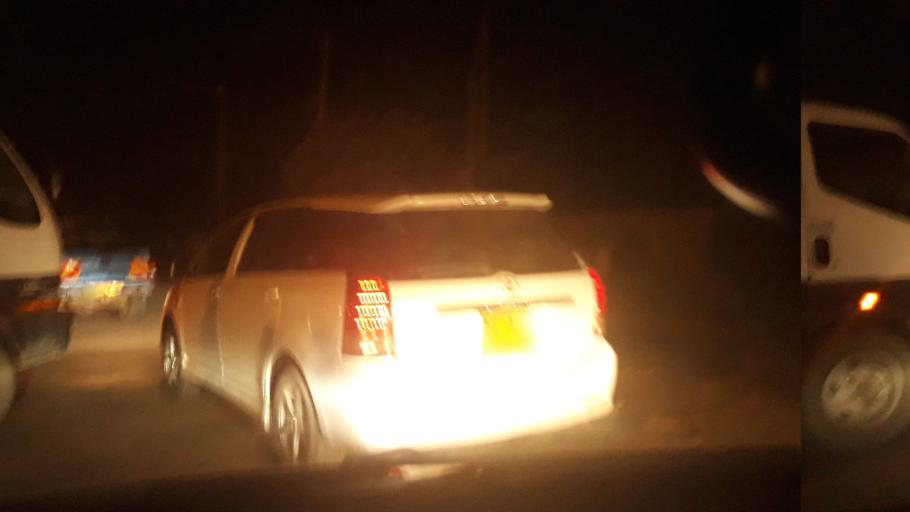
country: KE
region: Nairobi Area
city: Pumwani
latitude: -1.3011
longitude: 36.8853
